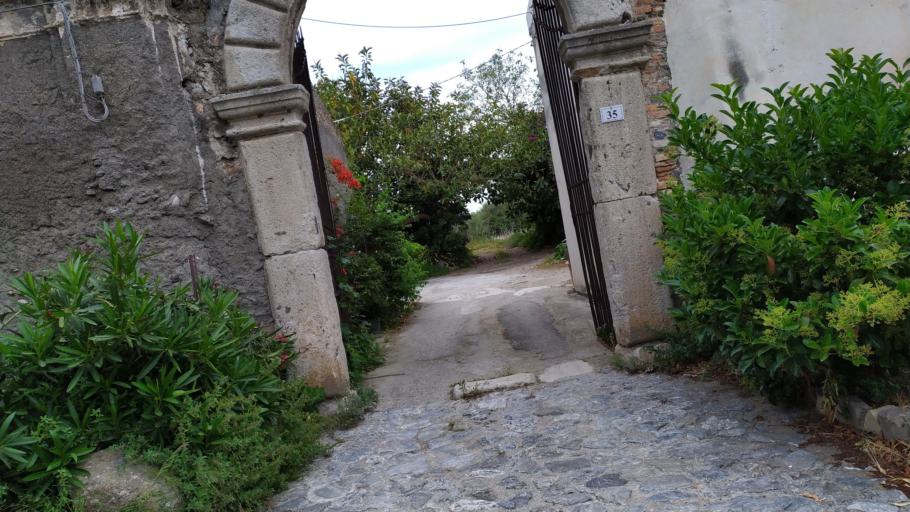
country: IT
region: Sicily
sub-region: Messina
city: San Filippo del Mela
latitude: 38.1792
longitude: 15.2653
